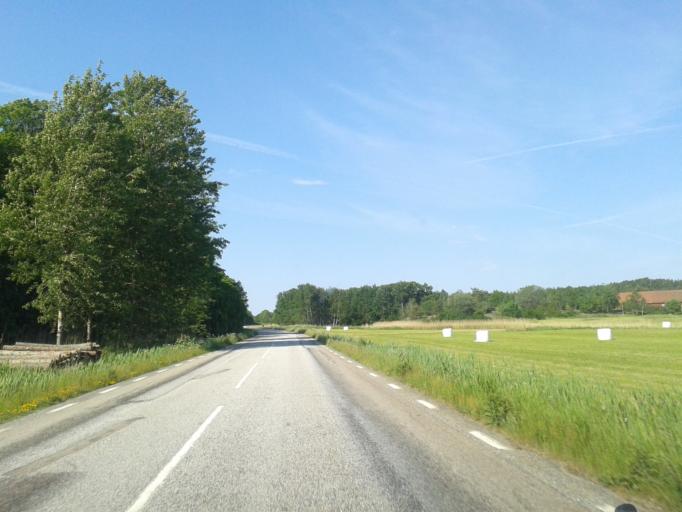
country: SE
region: Vaestra Goetaland
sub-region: Stromstads Kommun
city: Stroemstad
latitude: 58.8611
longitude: 11.2413
